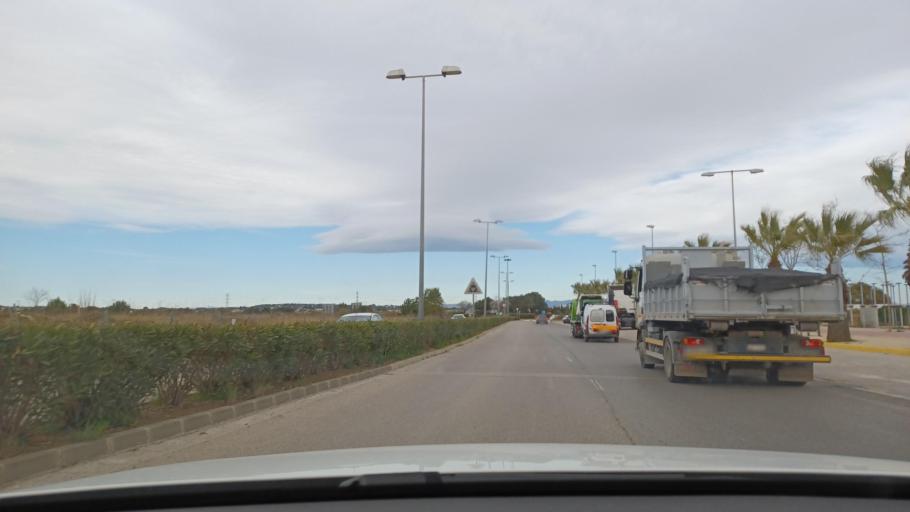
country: ES
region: Valencia
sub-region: Provincia de Valencia
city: Picassent
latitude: 39.3671
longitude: -0.4601
